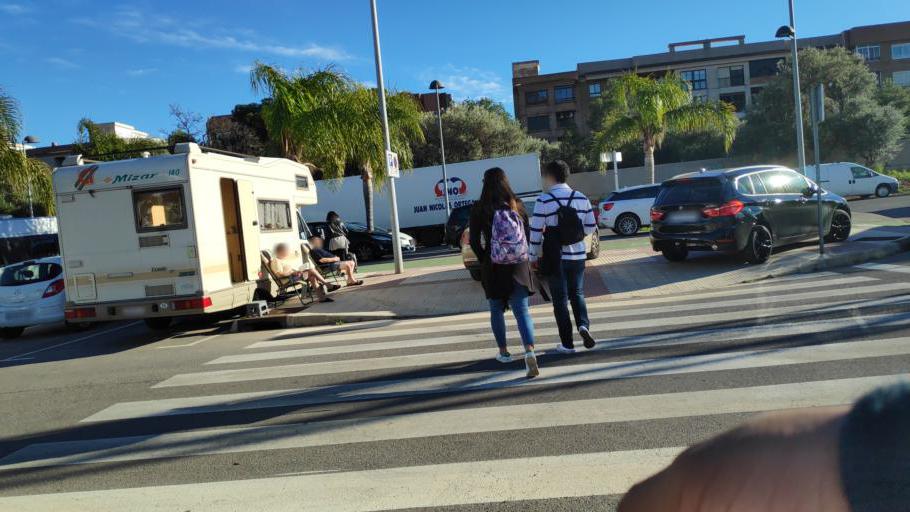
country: ES
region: Valencia
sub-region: Provincia de Castello
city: Benicassim
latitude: 40.0559
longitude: 0.0605
